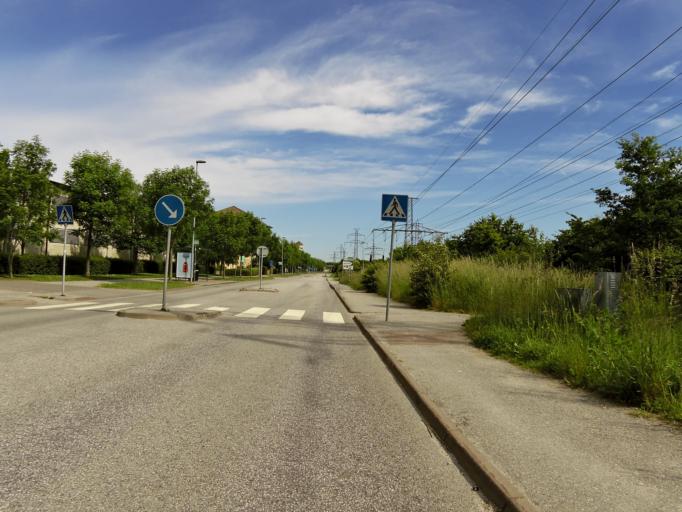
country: SE
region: Skane
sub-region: Lunds Kommun
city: Lund
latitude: 55.7047
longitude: 13.1611
